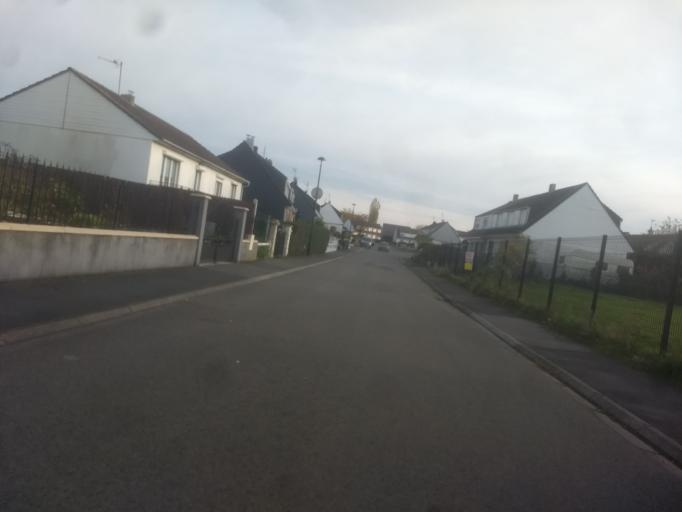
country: FR
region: Nord-Pas-de-Calais
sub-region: Departement du Pas-de-Calais
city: Beaurains
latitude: 50.2702
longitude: 2.7788
